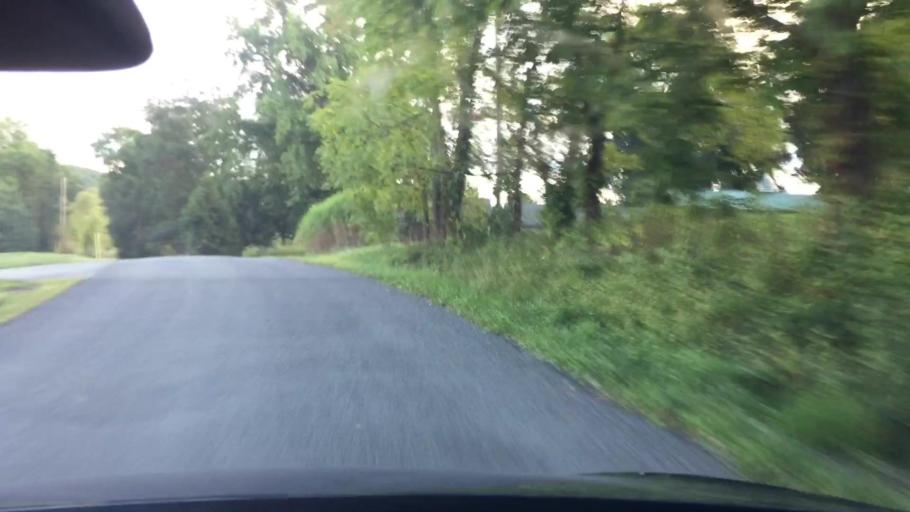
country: US
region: Pennsylvania
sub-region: Butler County
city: Saxonburg
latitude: 40.7377
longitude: -79.8764
